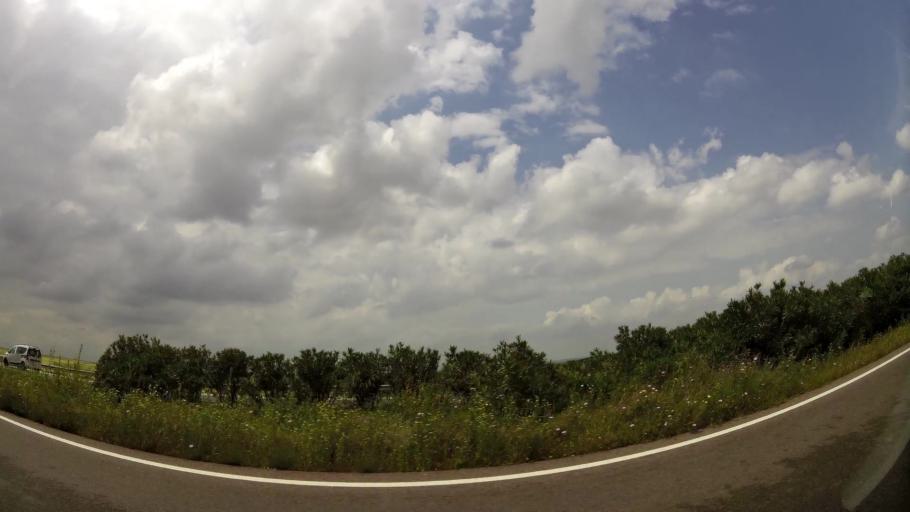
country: MA
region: Rabat-Sale-Zemmour-Zaer
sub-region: Khemisset
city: Tiflet
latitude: 33.9076
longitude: -6.4088
